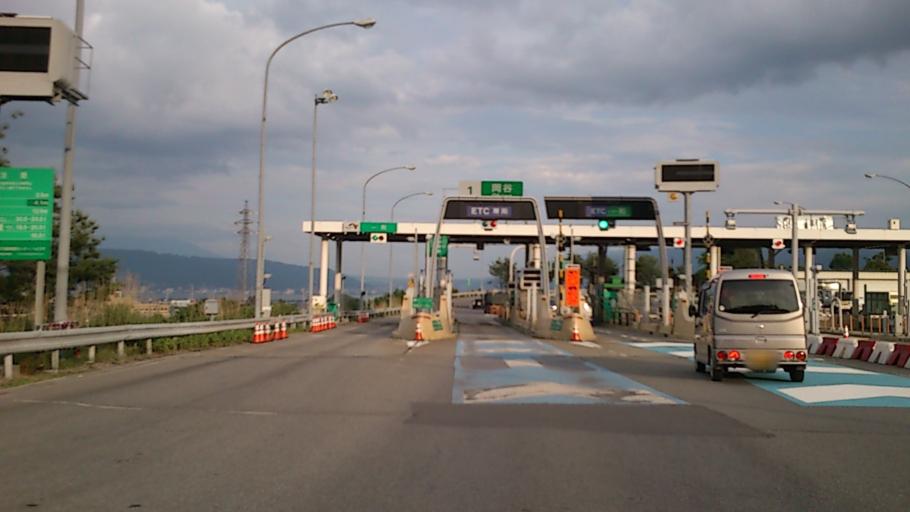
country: JP
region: Nagano
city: Okaya
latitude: 36.0840
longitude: 138.0399
